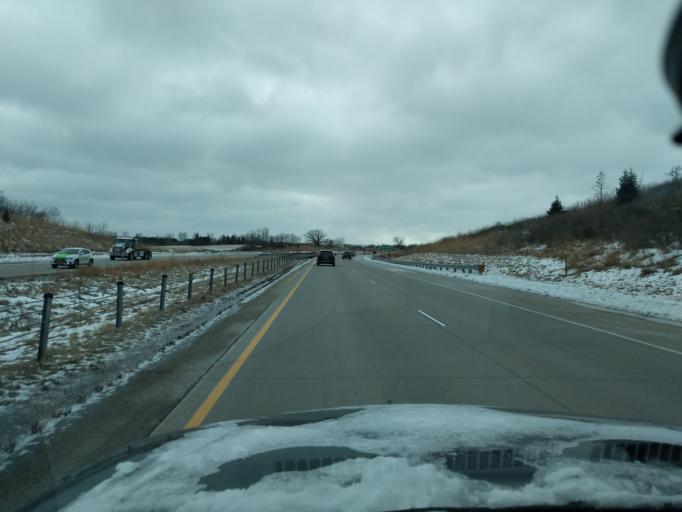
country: US
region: Minnesota
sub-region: Scott County
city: Shakopee
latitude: 44.8264
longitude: -93.5618
